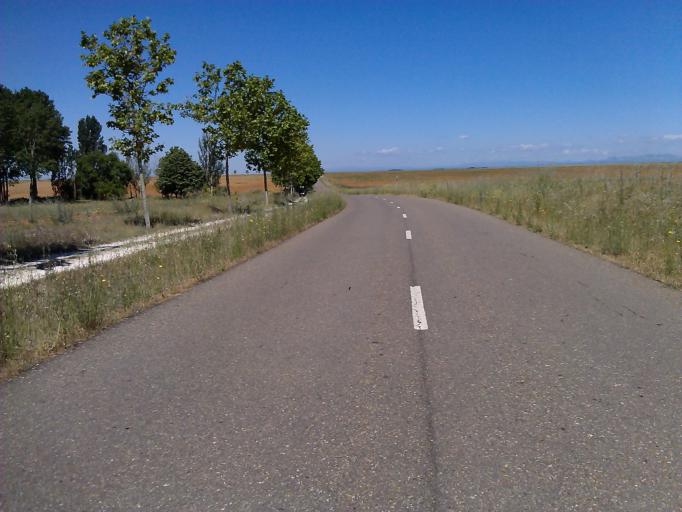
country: ES
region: Castille and Leon
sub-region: Provincia de Leon
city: Villamoratiel de las Matas
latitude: 42.4584
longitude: -5.2932
